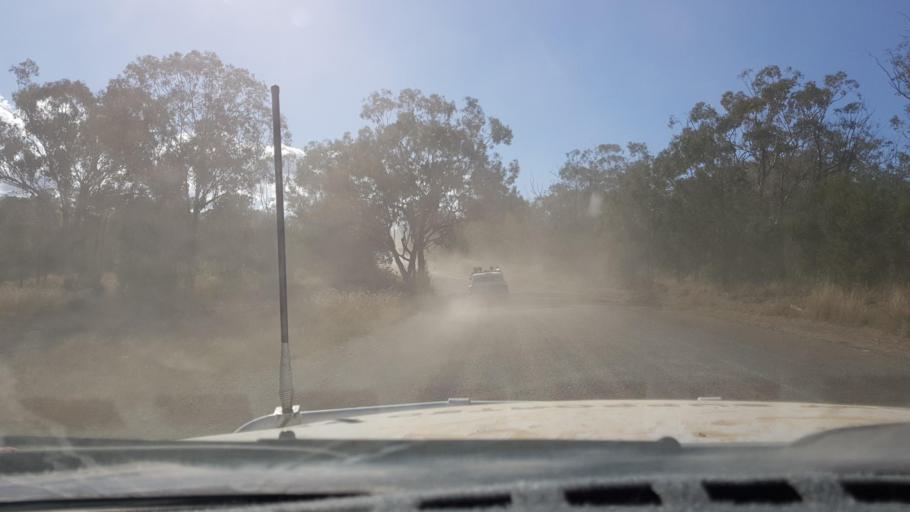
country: AU
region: New South Wales
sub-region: Tamworth Municipality
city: Manilla
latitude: -30.6577
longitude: 150.4839
